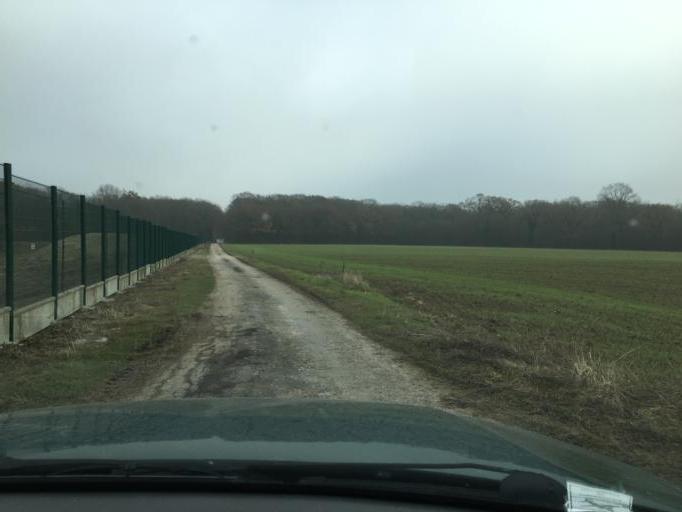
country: FR
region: Centre
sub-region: Departement du Loiret
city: Gidy
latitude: 47.9743
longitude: 1.8479
